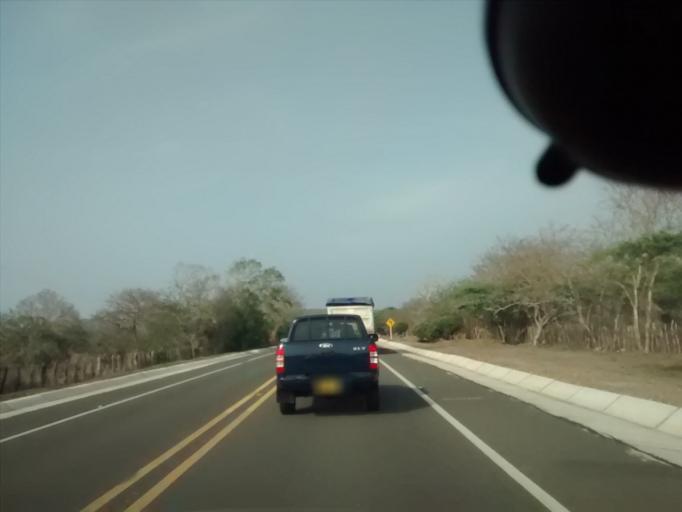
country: CO
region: Atlantico
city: Piojo
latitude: 10.8459
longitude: -75.1330
